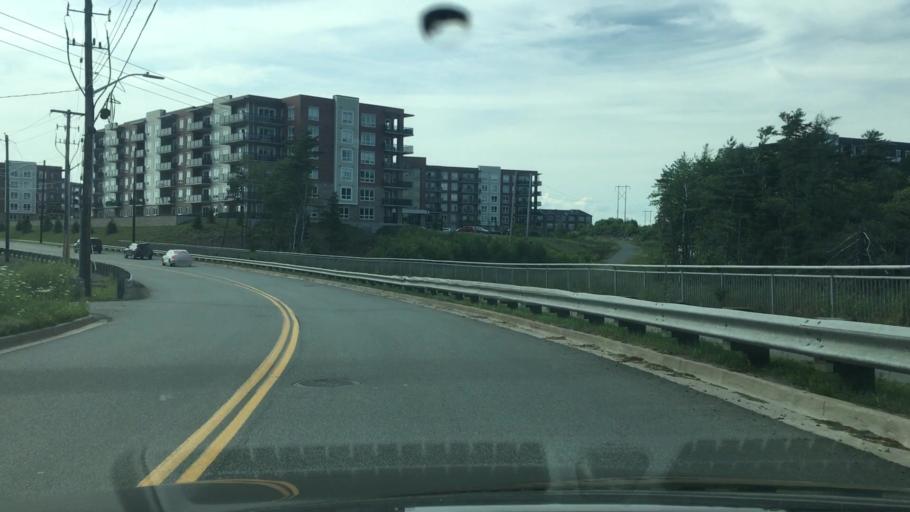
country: CA
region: Nova Scotia
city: Dartmouth
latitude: 44.6993
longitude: -63.6951
